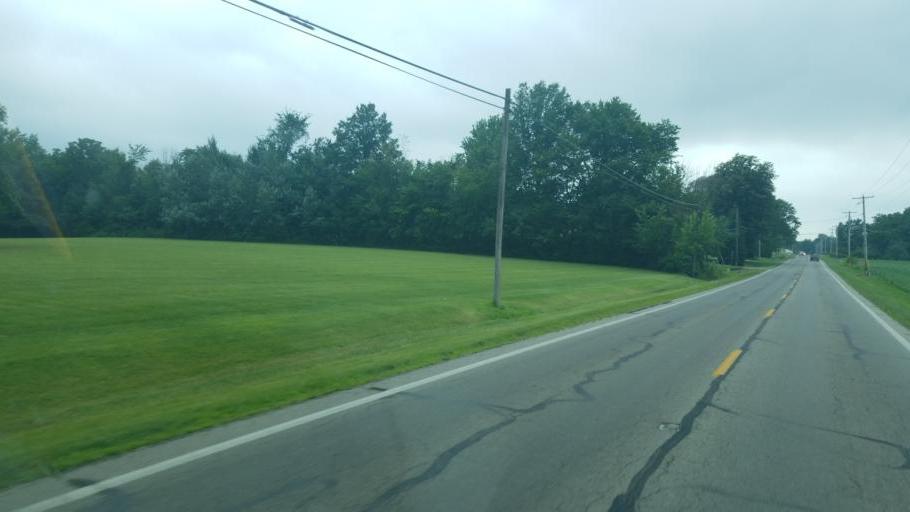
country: US
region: Ohio
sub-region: Logan County
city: Russells Point
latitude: 40.5236
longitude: -83.8724
